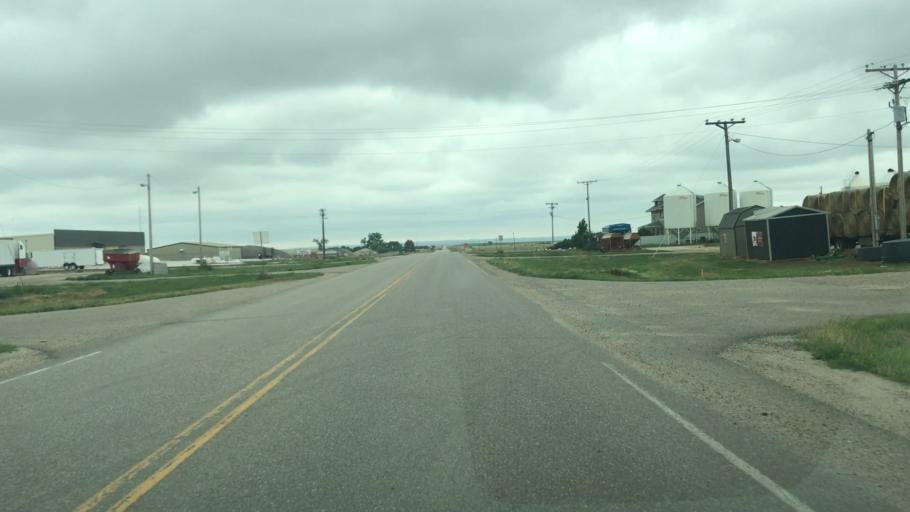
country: US
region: South Dakota
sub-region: Jackson County
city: Kadoka
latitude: 43.8355
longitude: -101.5225
